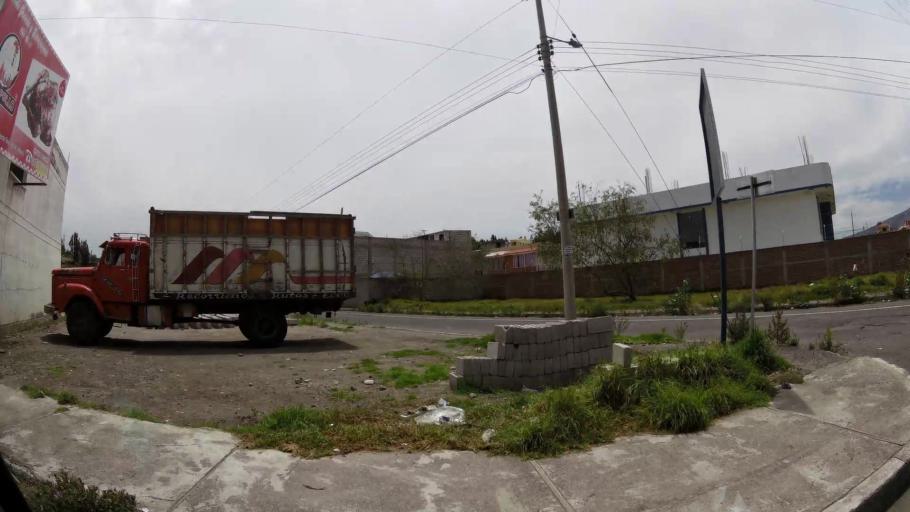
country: EC
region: Cotopaxi
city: San Miguel de Salcedo
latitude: -1.0496
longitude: -78.5952
